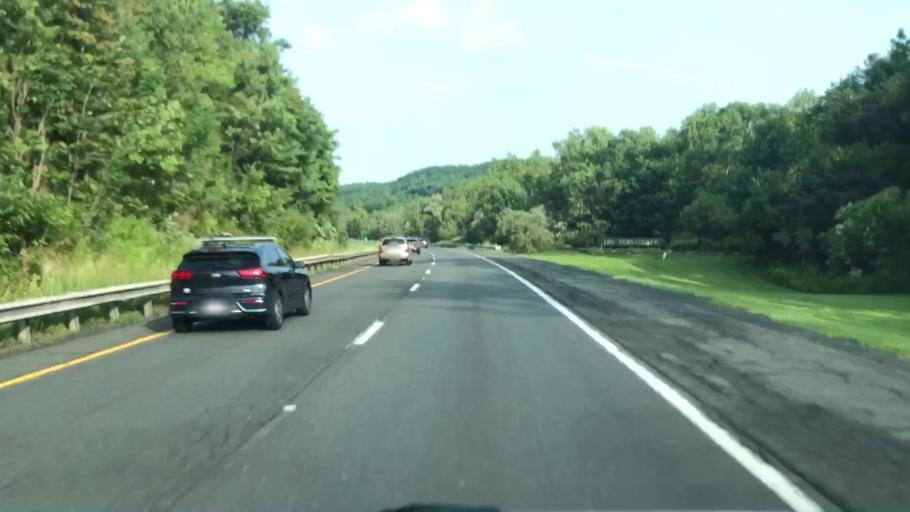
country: US
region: Massachusetts
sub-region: Berkshire County
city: Becket
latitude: 42.2892
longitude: -73.1576
